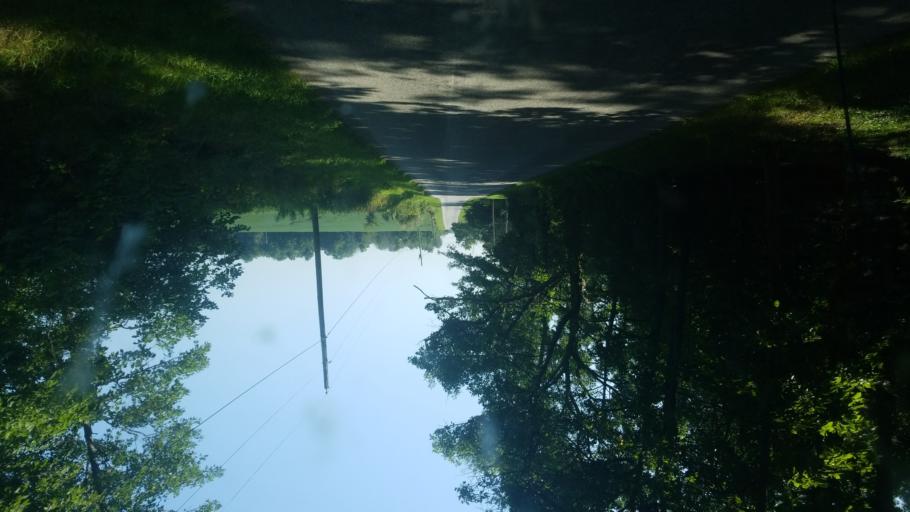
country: US
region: Ohio
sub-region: Lorain County
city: Wellington
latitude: 41.0624
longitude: -82.2016
